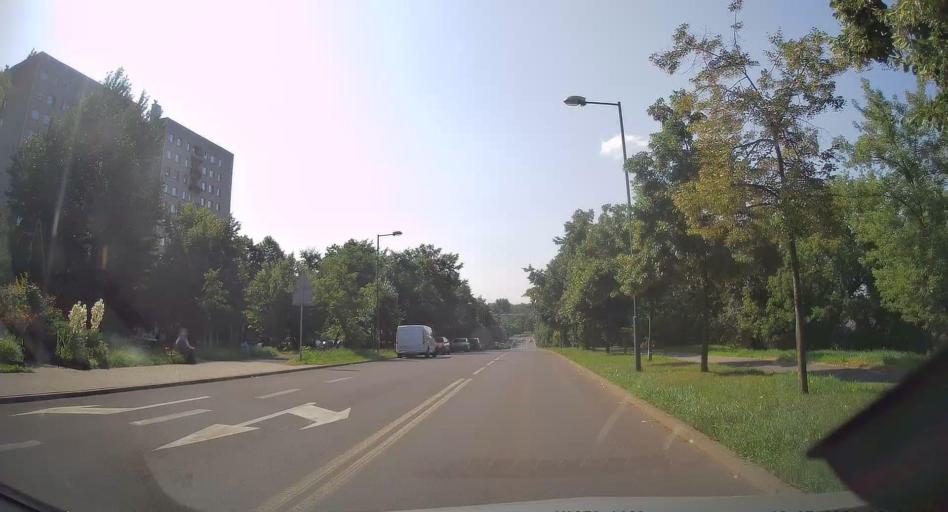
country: PL
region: Silesian Voivodeship
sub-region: Swietochlowice
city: Swietochlowice
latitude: 50.3100
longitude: 18.9112
